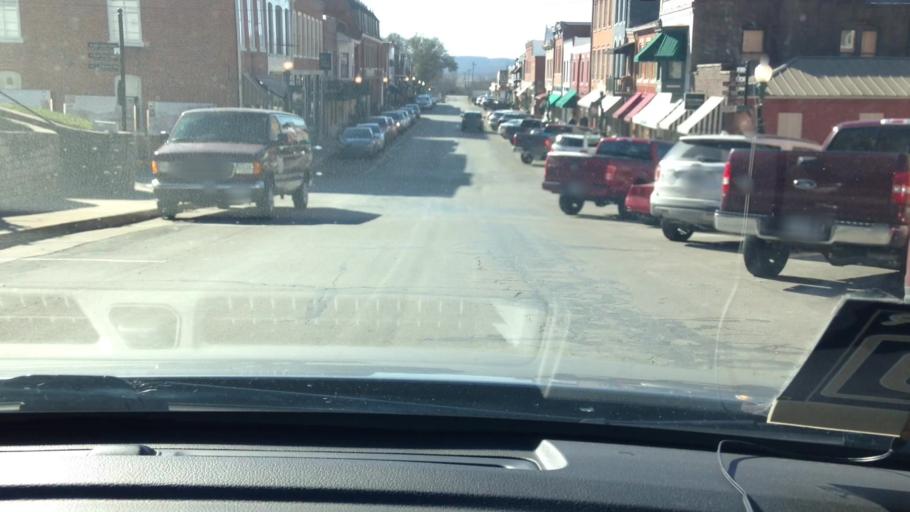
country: US
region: Missouri
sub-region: Platte County
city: Weston
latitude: 39.4120
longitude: -94.9010
